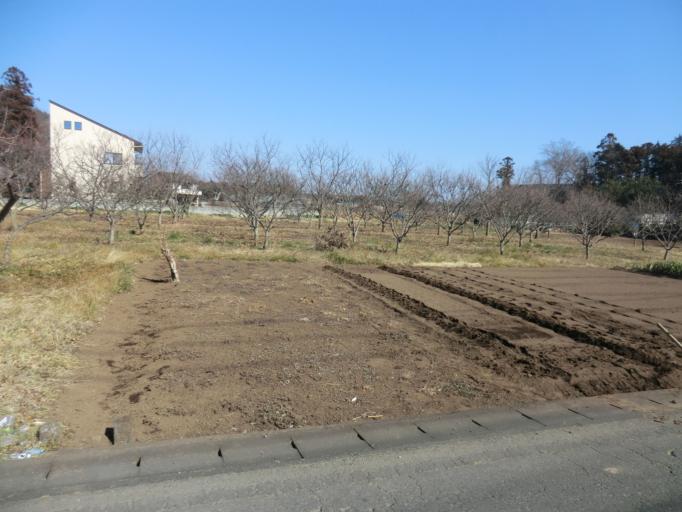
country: JP
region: Ibaraki
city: Naka
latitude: 36.0355
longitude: 140.1259
